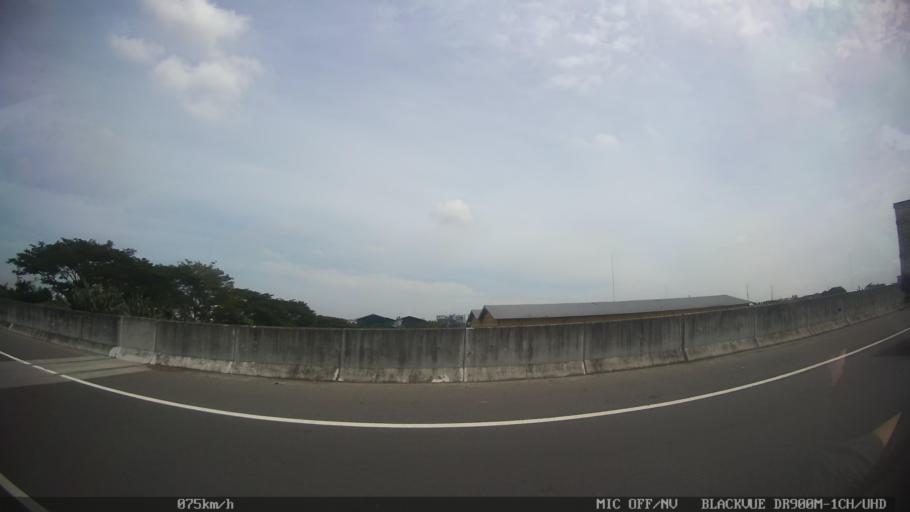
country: ID
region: North Sumatra
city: Medan
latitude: 3.6494
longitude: 98.6593
